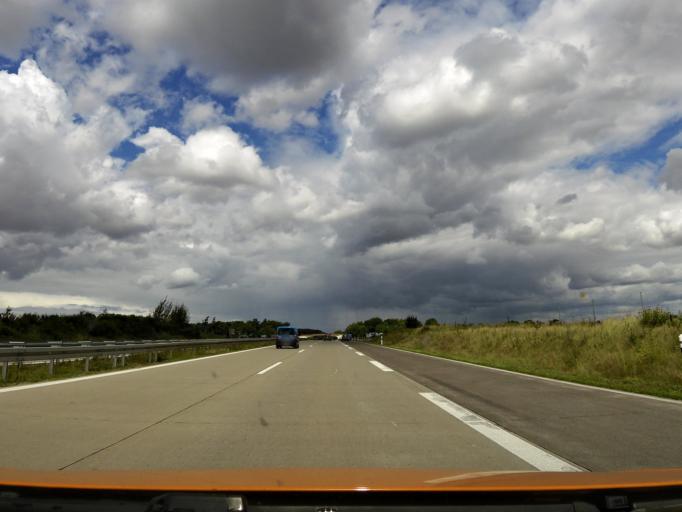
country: DE
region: Brandenburg
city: Gerswalde
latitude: 53.0892
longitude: 13.8496
